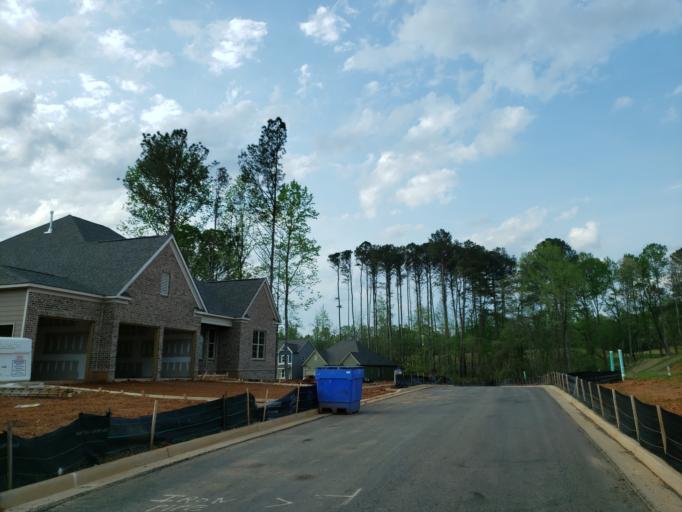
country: US
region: Georgia
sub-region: Cherokee County
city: Holly Springs
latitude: 34.1703
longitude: -84.4324
